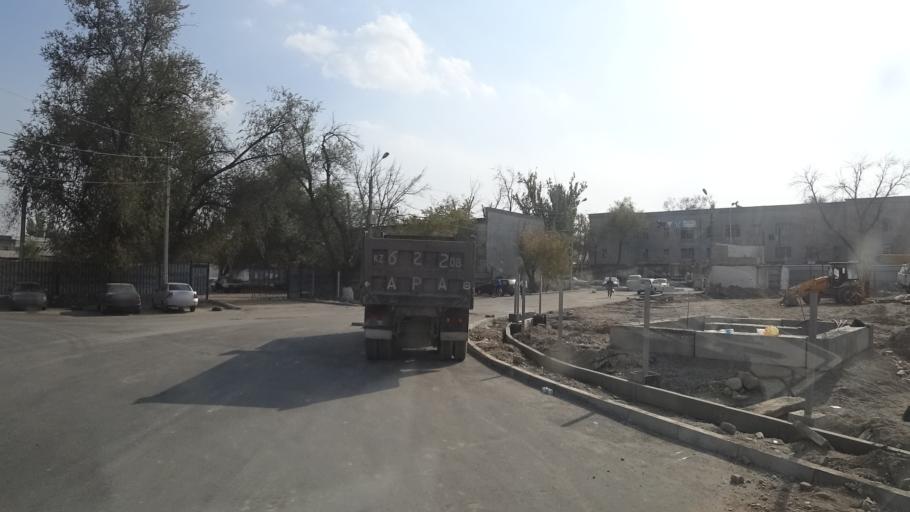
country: KZ
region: Zhambyl
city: Taraz
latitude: 42.8995
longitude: 71.3960
